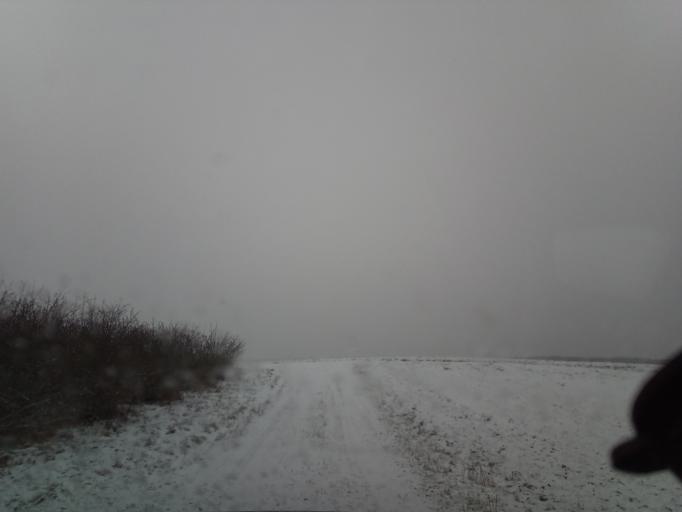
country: LT
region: Utenos apskritis
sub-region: Anyksciai
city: Anyksciai
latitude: 55.4061
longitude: 25.1711
